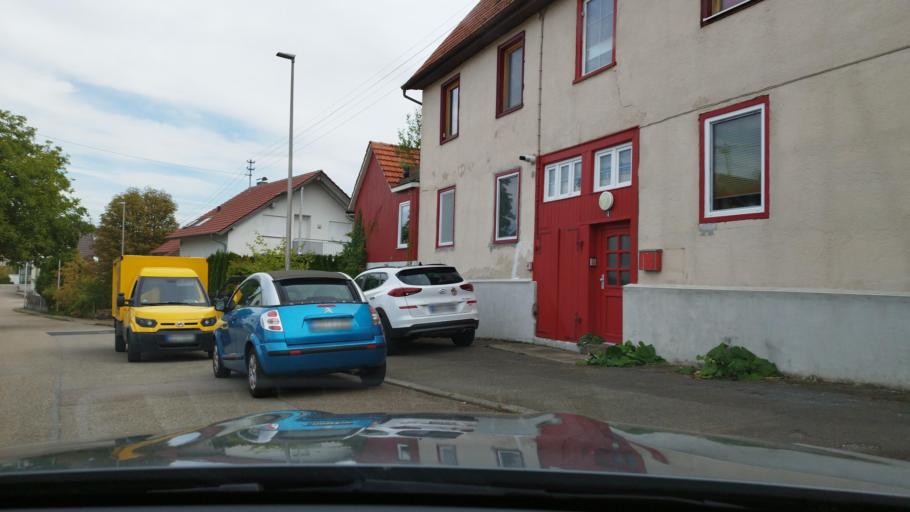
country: DE
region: Baden-Wuerttemberg
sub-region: Regierungsbezirk Stuttgart
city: Burgstetten
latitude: 48.9174
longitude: 9.3704
